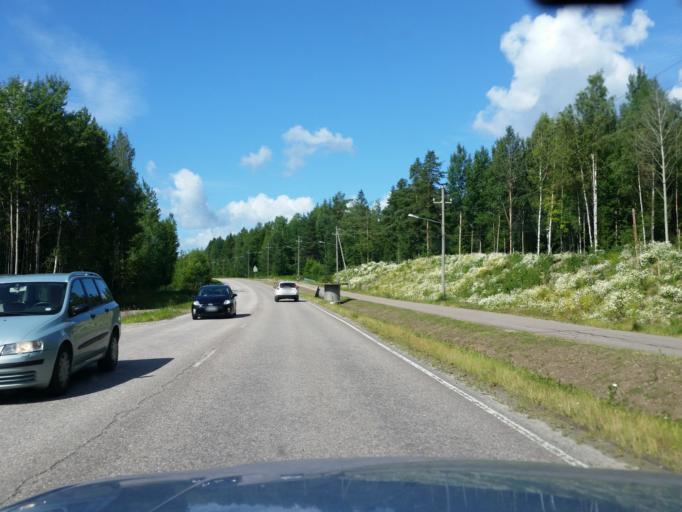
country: FI
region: Uusimaa
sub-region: Helsinki
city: Vihti
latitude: 60.3271
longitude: 24.3039
